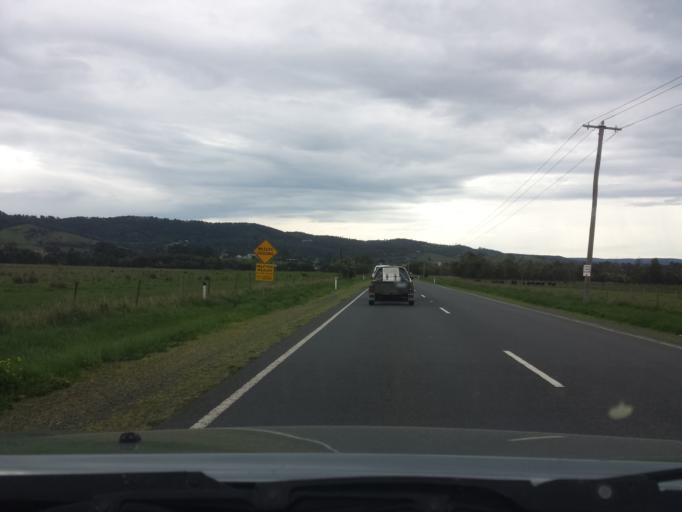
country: AU
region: Victoria
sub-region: Yarra Ranges
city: Yarra Glen
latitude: -37.6683
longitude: 145.3792
